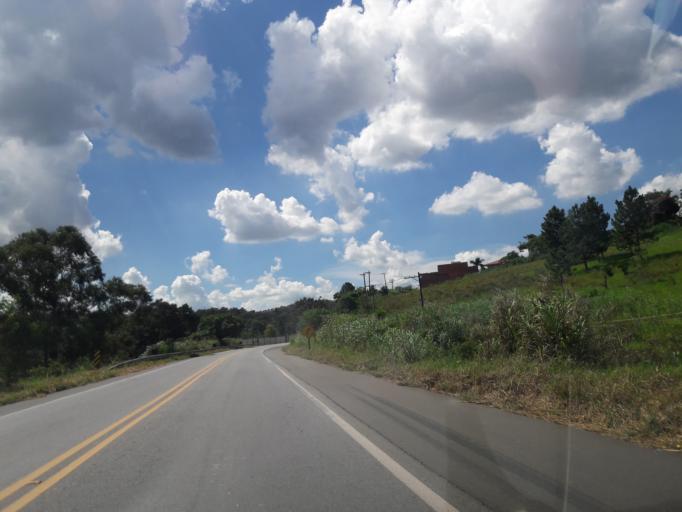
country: BR
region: Sao Paulo
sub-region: Campo Limpo Paulista
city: Campo Limpo Paulista
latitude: -23.2330
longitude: -46.7913
